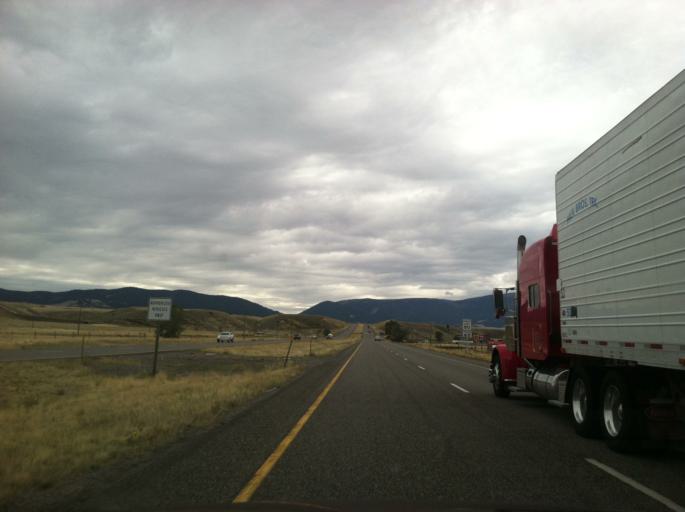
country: US
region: Montana
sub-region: Park County
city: Livingston
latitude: 45.6811
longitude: -110.5093
